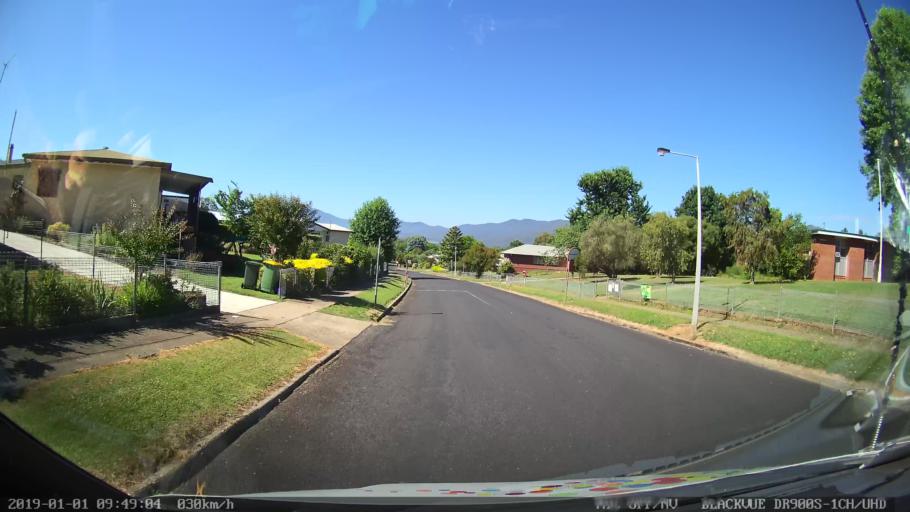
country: AU
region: New South Wales
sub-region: Snowy River
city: Jindabyne
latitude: -36.2141
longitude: 148.1324
